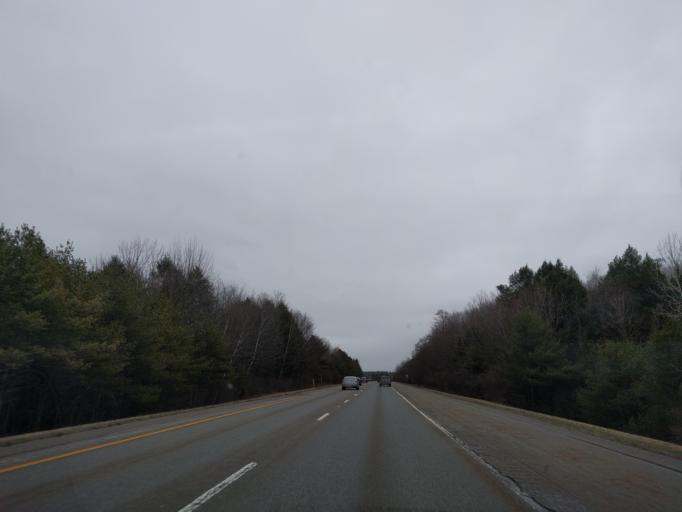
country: US
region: Massachusetts
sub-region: Worcester County
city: Templeton
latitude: 42.5614
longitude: -72.0532
